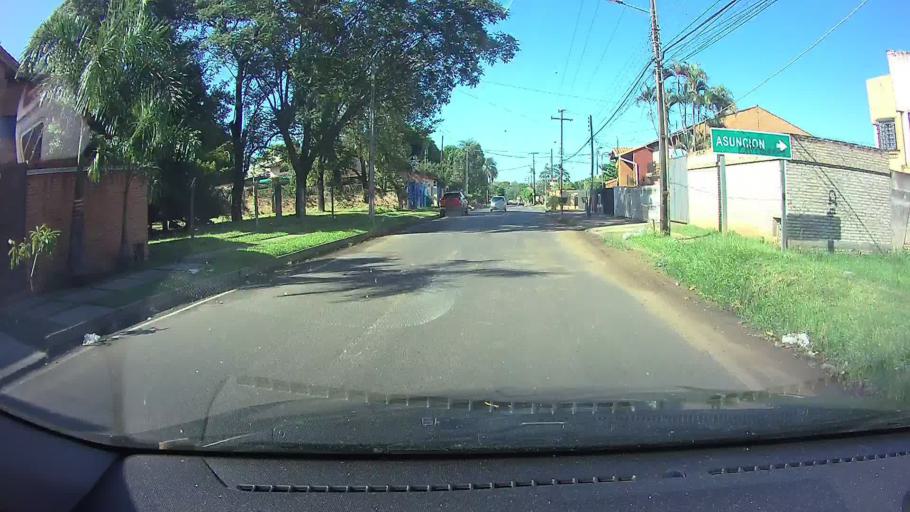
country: PY
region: Central
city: Fernando de la Mora
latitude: -25.2665
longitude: -57.5146
